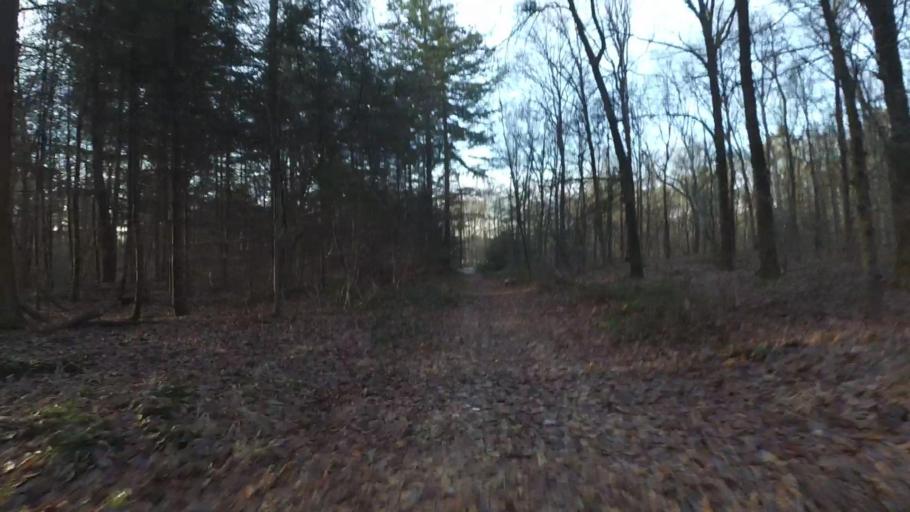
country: NL
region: Utrecht
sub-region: Gemeente Utrechtse Heuvelrug
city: Maarn
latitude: 52.0867
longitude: 5.3413
